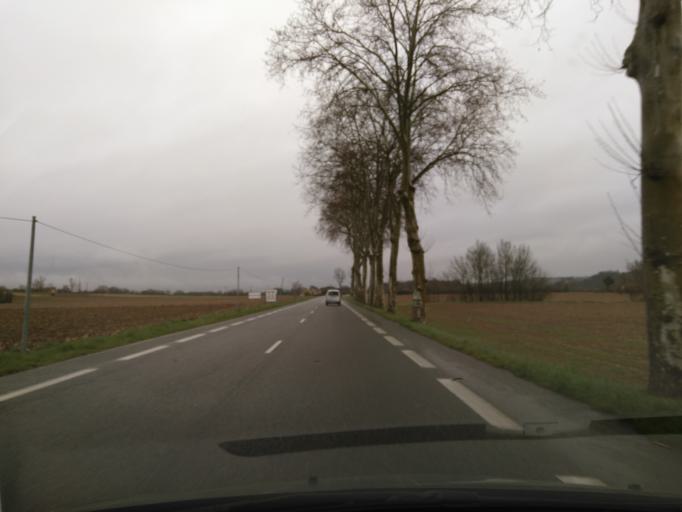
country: FR
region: Midi-Pyrenees
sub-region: Departement de la Haute-Garonne
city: Rieux-Volvestre
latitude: 43.2700
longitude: 1.1978
